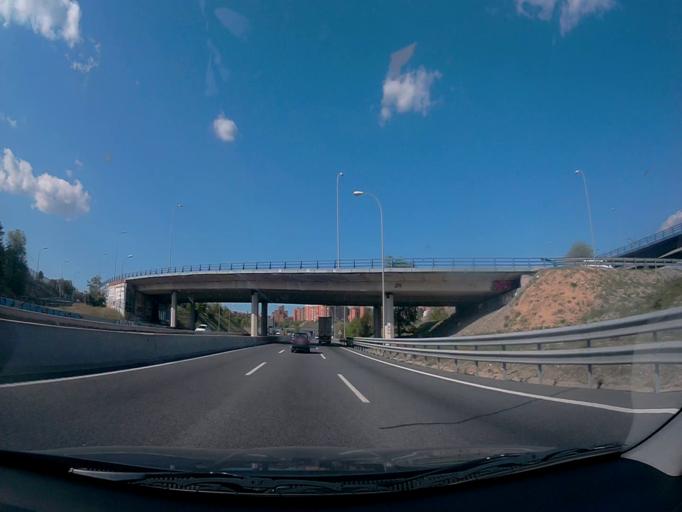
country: ES
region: Madrid
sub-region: Provincia de Madrid
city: Puente de Vallecas
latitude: 40.3720
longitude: -3.6537
